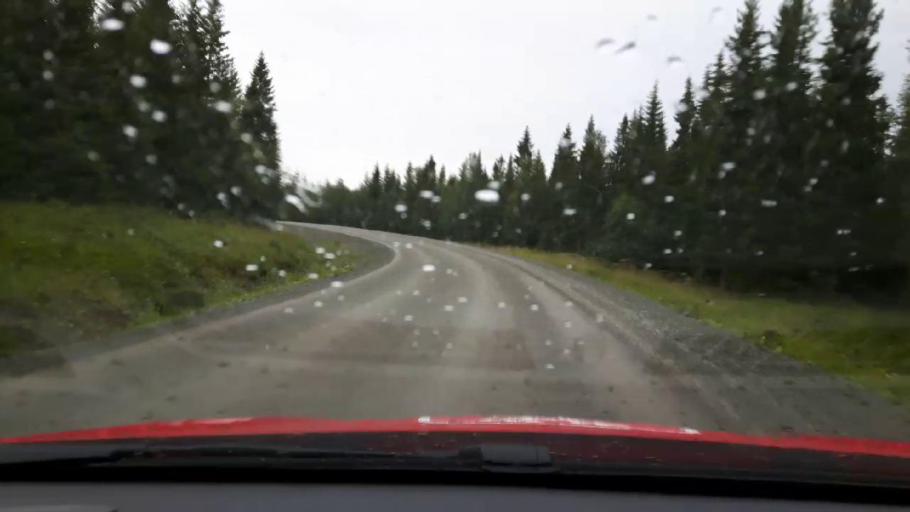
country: SE
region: Jaemtland
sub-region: Are Kommun
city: Are
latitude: 63.4503
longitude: 12.6553
